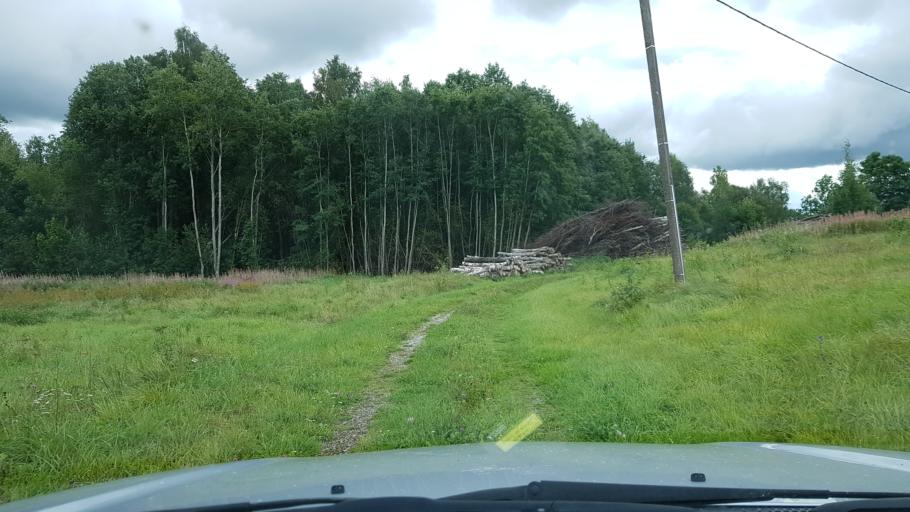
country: EE
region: Harju
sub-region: Raasiku vald
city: Arukula
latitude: 59.2699
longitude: 25.1041
